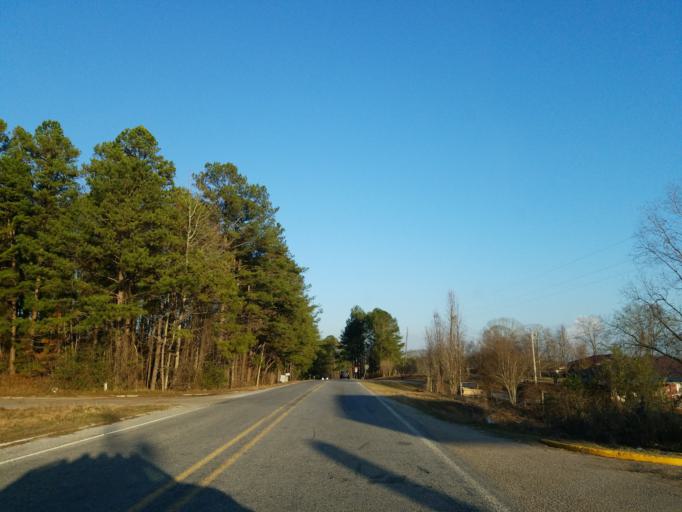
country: US
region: Mississippi
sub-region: Clarke County
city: Stonewall
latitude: 32.1642
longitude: -88.8646
